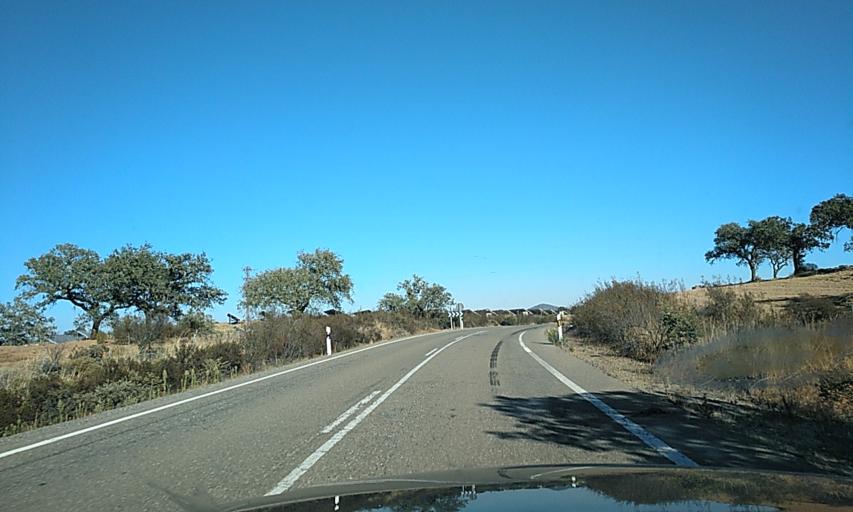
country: ES
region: Andalusia
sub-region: Provincia de Huelva
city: Santa Barbara de Casa
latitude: 37.7801
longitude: -7.1560
